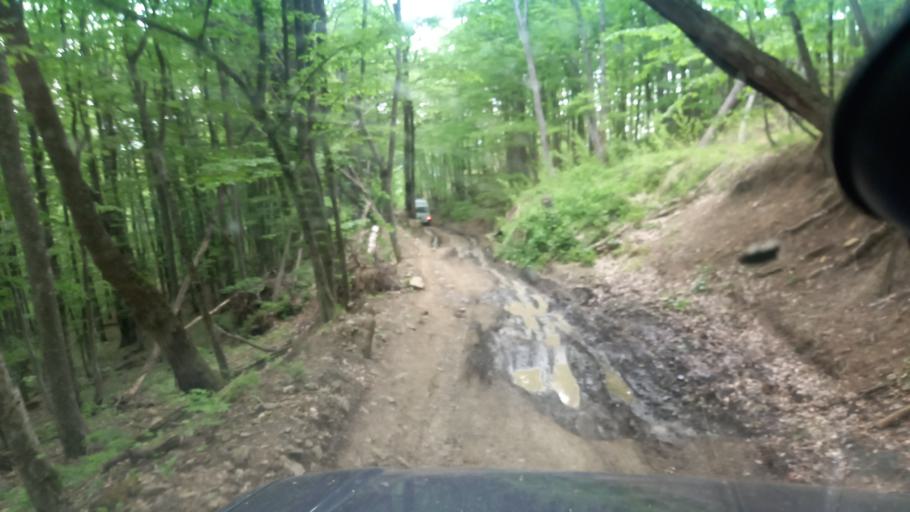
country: RU
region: Krasnodarskiy
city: Tuapse
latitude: 44.2508
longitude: 39.2825
